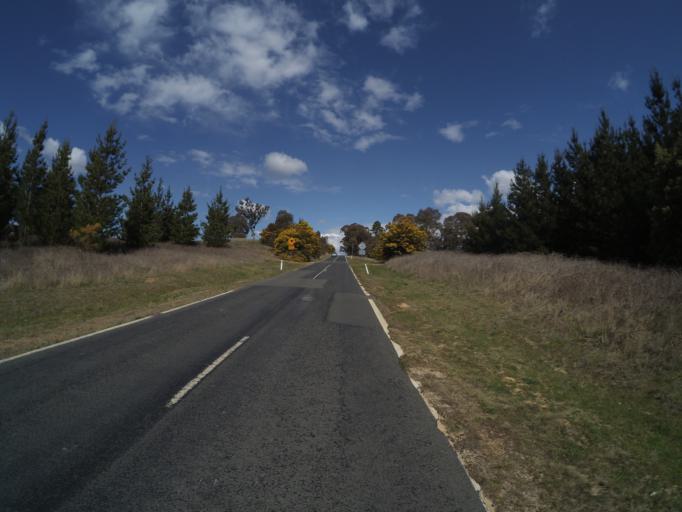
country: AU
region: Australian Capital Territory
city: Macquarie
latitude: -35.3766
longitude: 148.9617
